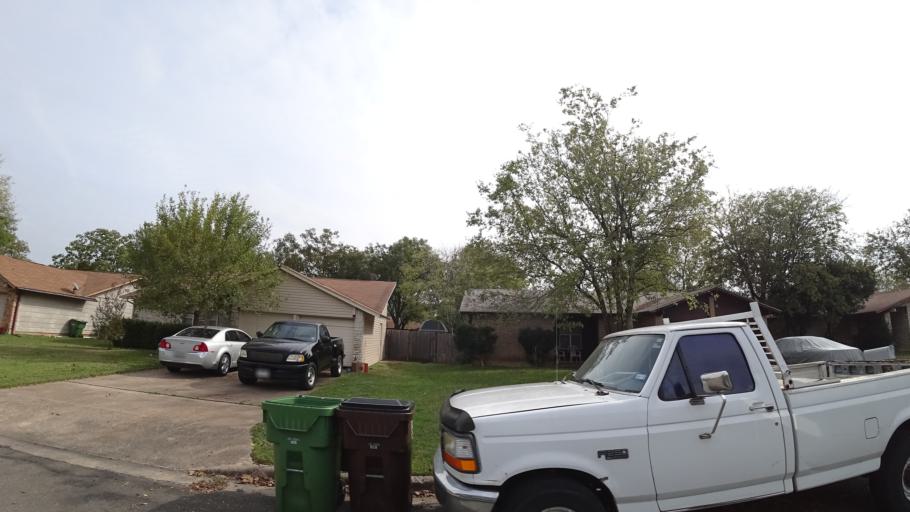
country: US
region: Texas
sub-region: Williamson County
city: Round Rock
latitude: 30.4962
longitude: -97.6870
